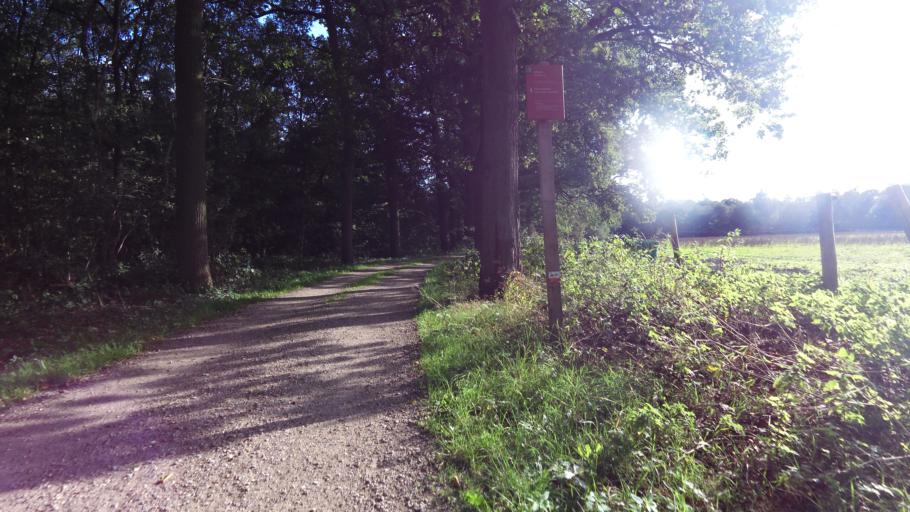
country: NL
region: Gelderland
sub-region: Gemeente Renkum
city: Renkum
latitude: 51.9902
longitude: 5.7280
